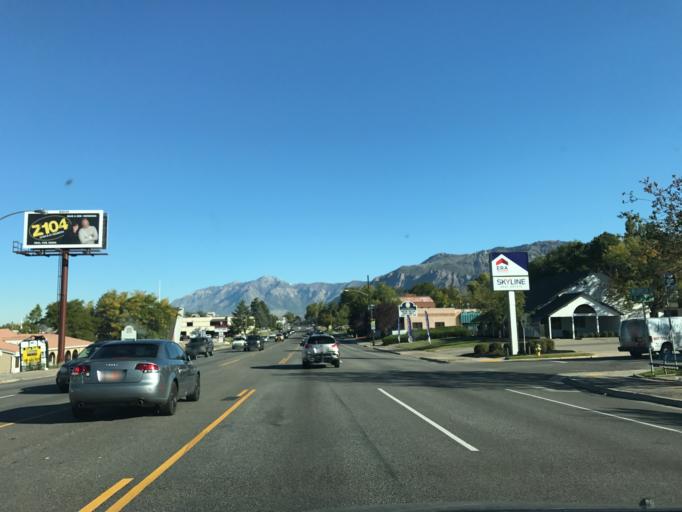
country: US
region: Utah
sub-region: Weber County
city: South Ogden
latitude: 41.2012
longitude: -111.9486
